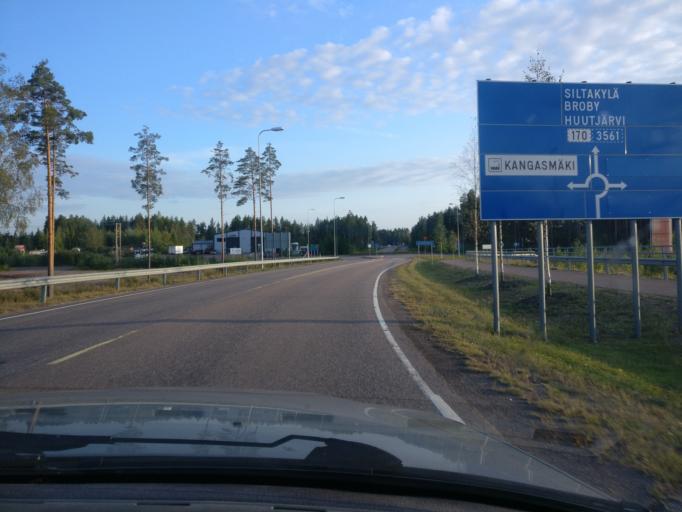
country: FI
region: Kymenlaakso
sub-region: Kotka-Hamina
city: Broby
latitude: 60.5024
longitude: 26.7422
